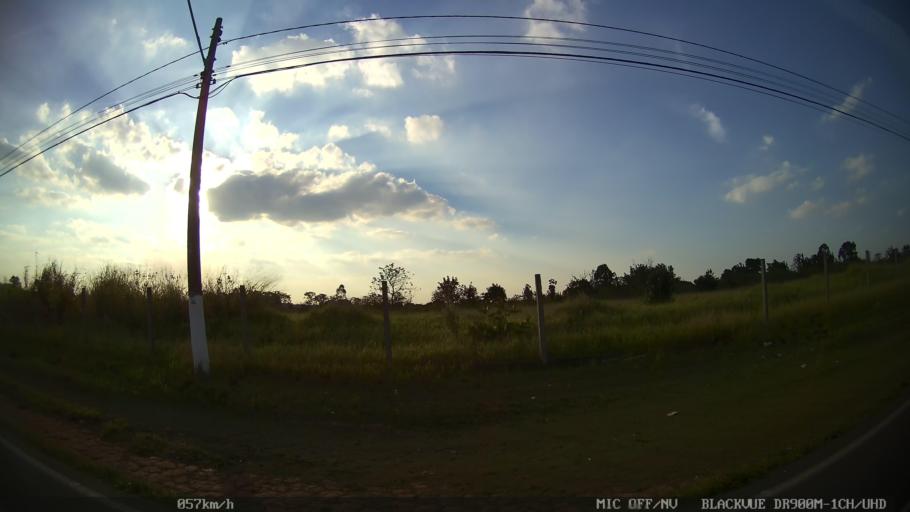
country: BR
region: Sao Paulo
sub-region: Hortolandia
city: Hortolandia
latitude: -22.8625
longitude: -47.1811
